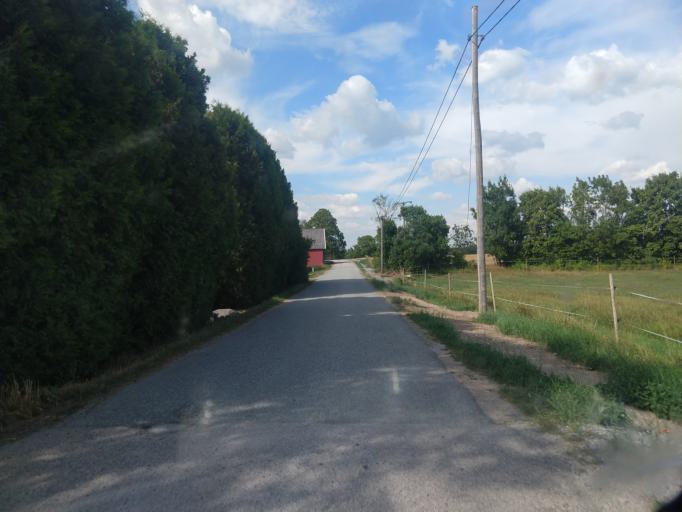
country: SE
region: Blekinge
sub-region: Karlskrona Kommun
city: Nattraby
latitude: 56.2502
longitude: 15.5266
